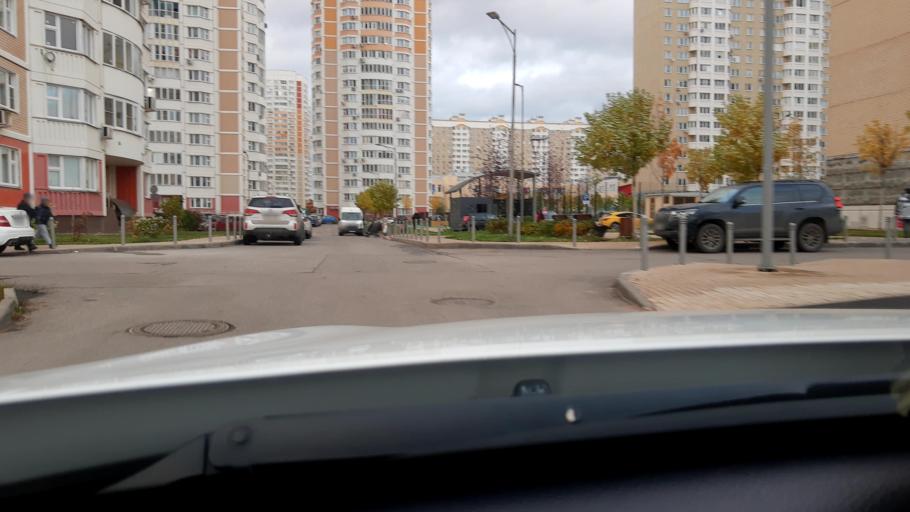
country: RU
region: Moskovskaya
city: Moskovskiy
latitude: 55.5985
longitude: 37.3604
